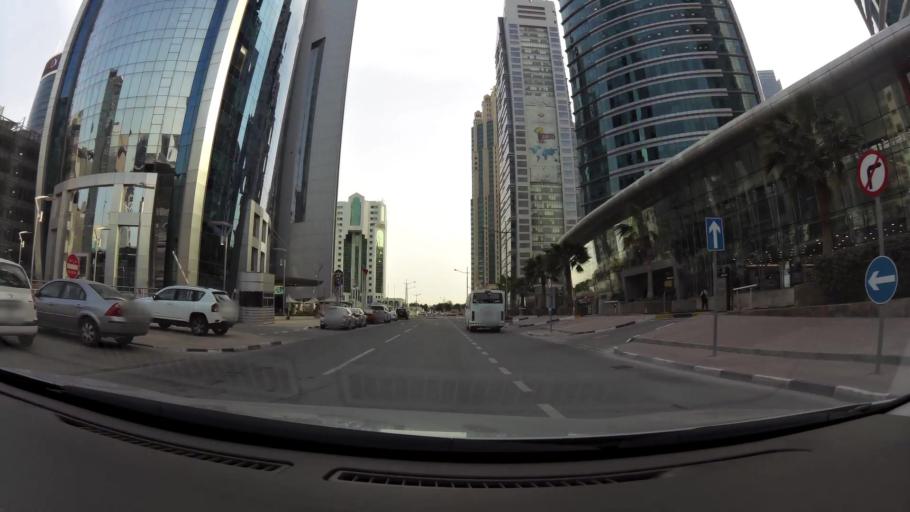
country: QA
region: Baladiyat ad Dawhah
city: Doha
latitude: 25.3214
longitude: 51.5298
